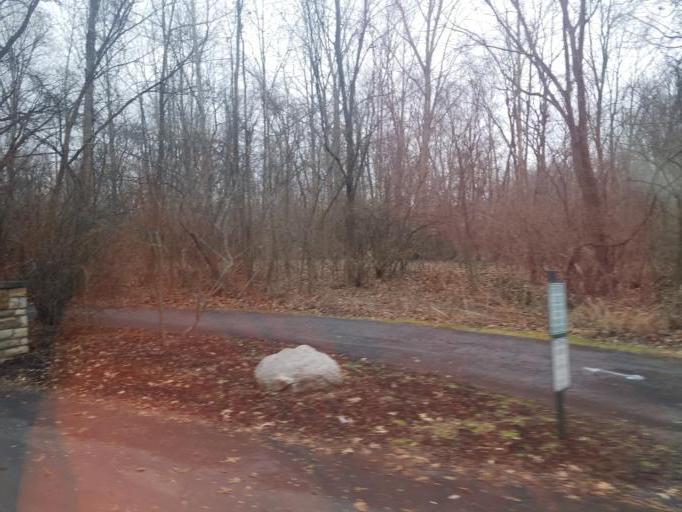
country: US
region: Ohio
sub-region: Franklin County
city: Westerville
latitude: 40.1289
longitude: -82.9458
